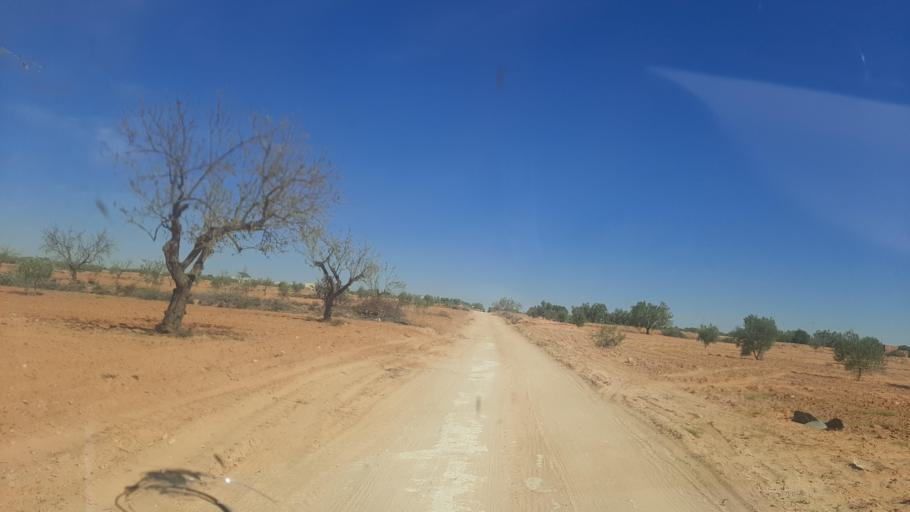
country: TN
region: Safaqis
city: Sfax
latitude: 34.8741
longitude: 10.5655
